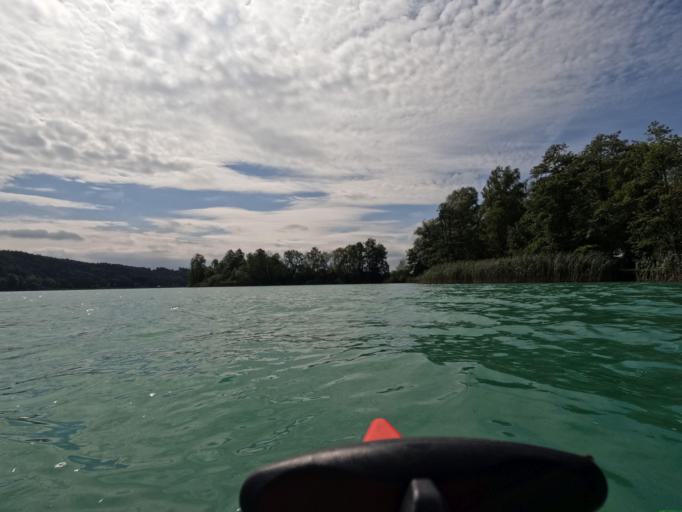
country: DE
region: Bavaria
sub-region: Upper Bavaria
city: Taching am See
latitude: 47.9791
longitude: 12.7403
